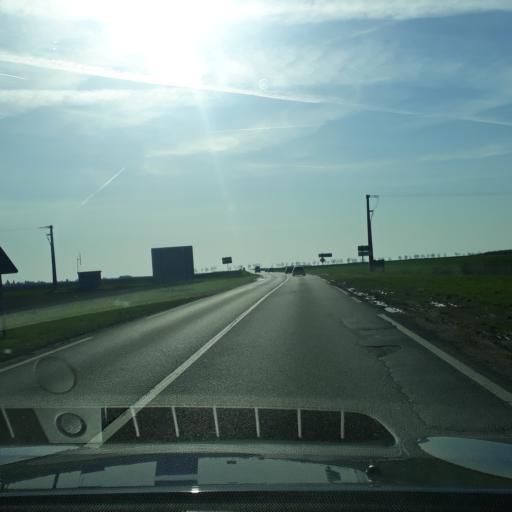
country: FR
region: Ile-de-France
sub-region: Departement de l'Essonne
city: Corbreuse
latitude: 48.4523
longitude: 1.9276
